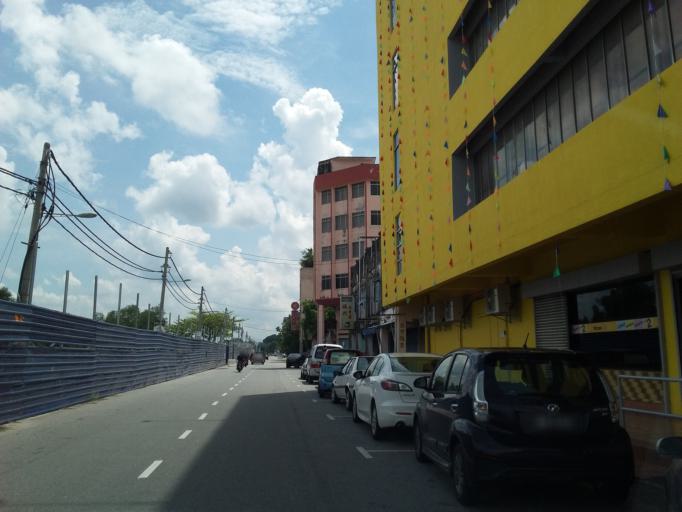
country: MY
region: Johor
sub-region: Daerah Batu Pahat
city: Batu Pahat
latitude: 1.8519
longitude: 102.9249
